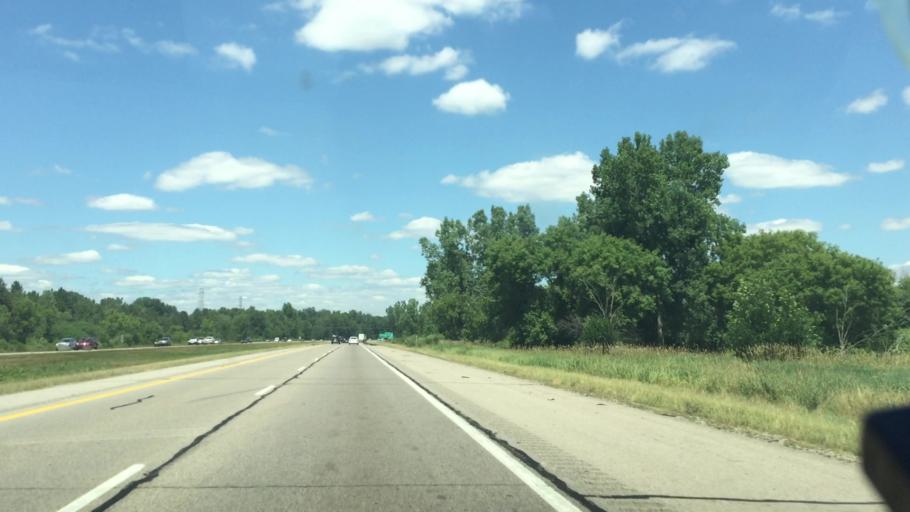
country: US
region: Michigan
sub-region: Washtenaw County
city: Ypsilanti
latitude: 42.3487
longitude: -83.5931
